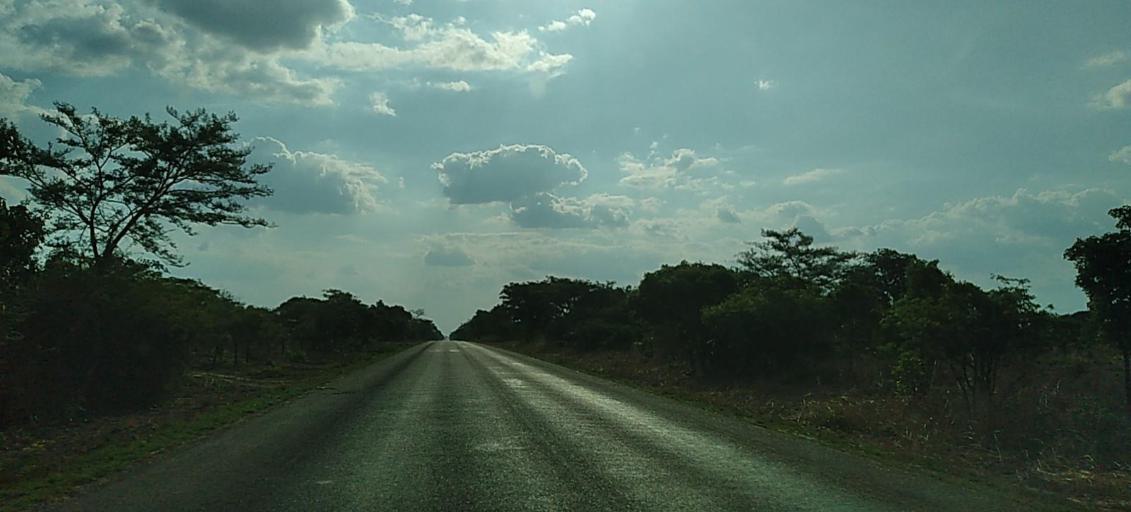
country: ZM
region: Copperbelt
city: Mpongwe
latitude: -13.3902
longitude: 28.3749
